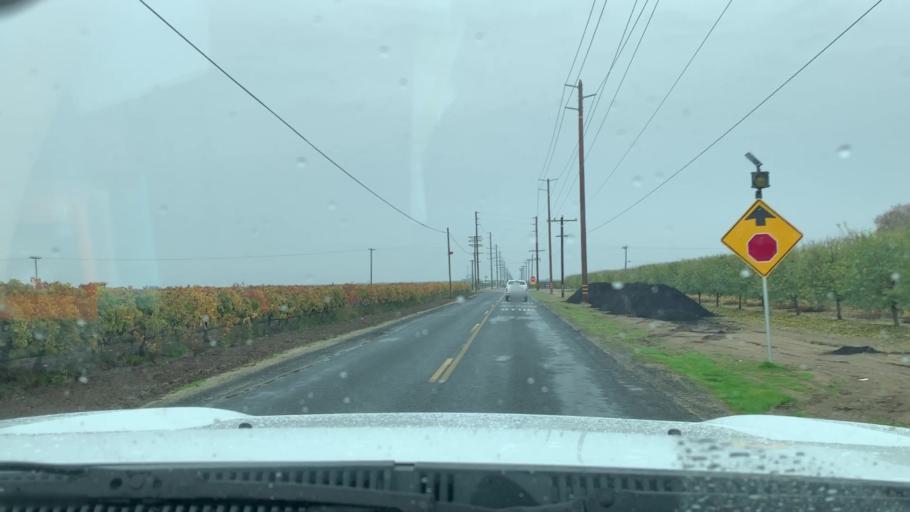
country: US
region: California
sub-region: Kern County
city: Delano
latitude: 35.8340
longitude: -119.2167
